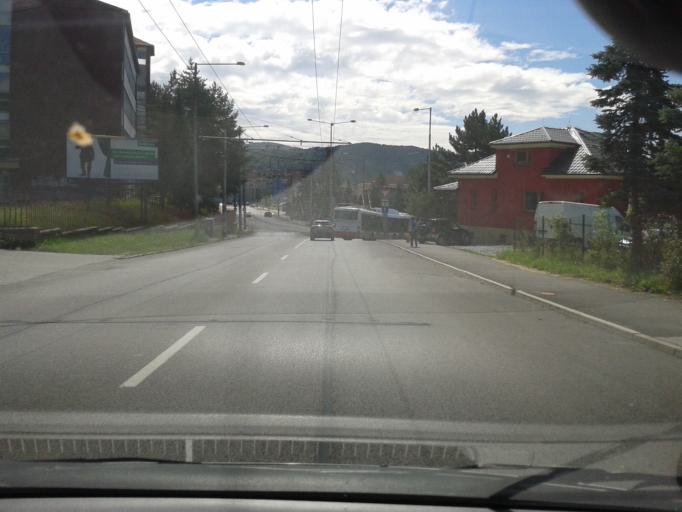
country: SK
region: Banskobystricky
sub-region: Okres Banska Bystrica
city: Banska Bystrica
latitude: 48.7414
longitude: 19.1247
